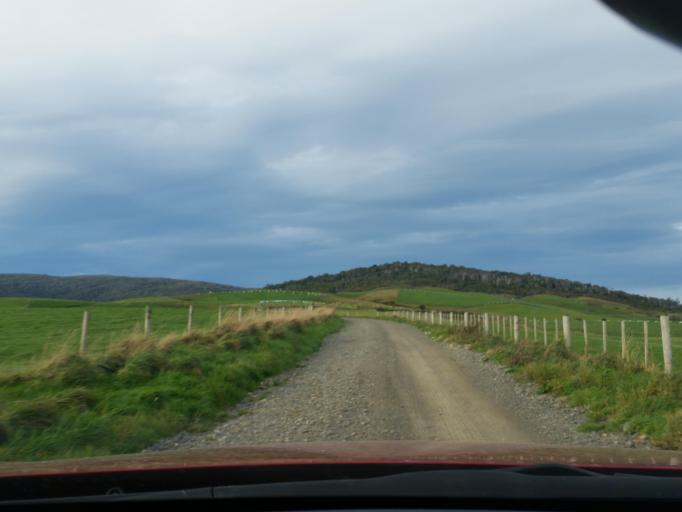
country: NZ
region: Southland
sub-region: Southland District
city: Riverton
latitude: -46.2958
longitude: 167.7706
